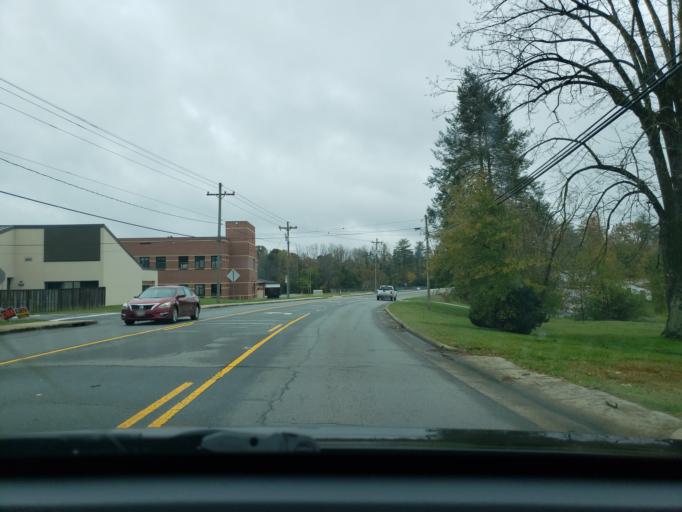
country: US
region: North Carolina
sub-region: Stokes County
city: Walnut Cove
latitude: 36.3111
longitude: -80.1396
